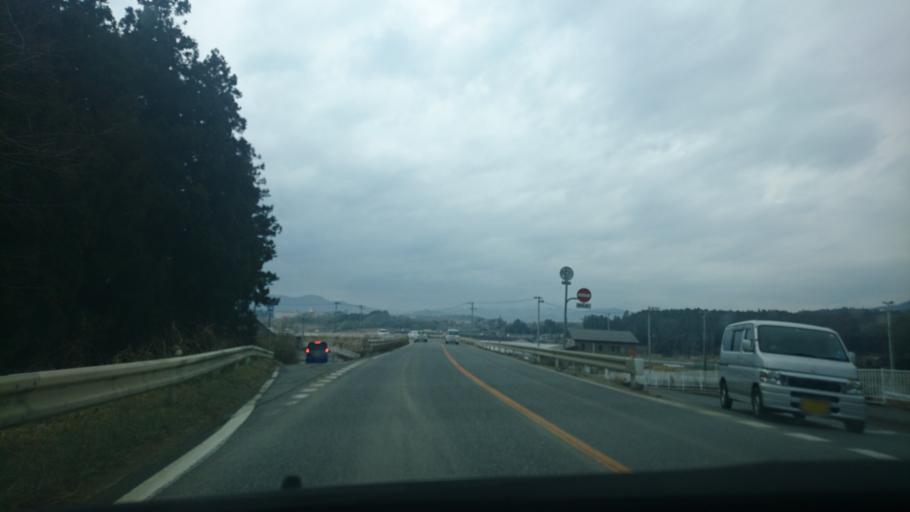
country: JP
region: Iwate
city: Ofunato
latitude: 39.0150
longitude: 141.6626
